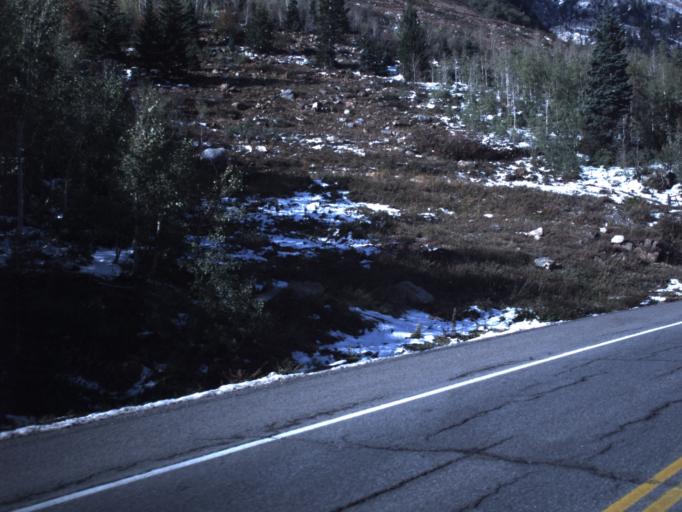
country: US
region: Utah
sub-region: Salt Lake County
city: Granite
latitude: 40.5822
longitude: -111.6588
